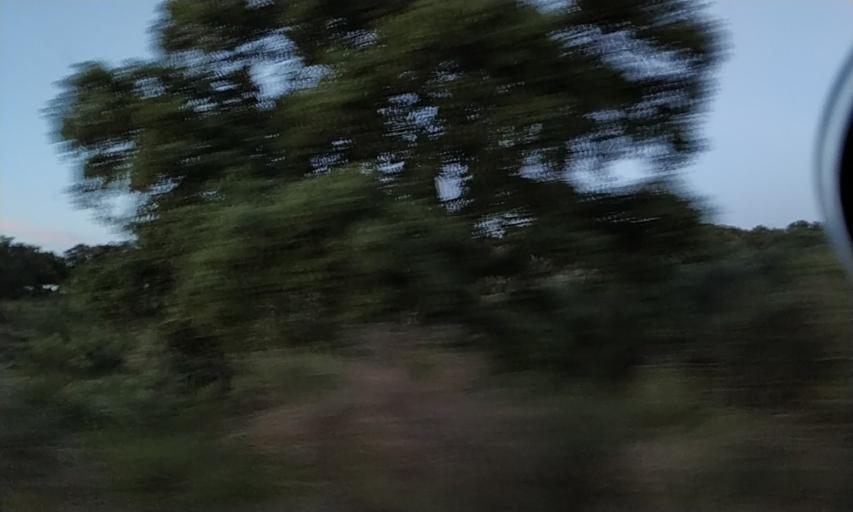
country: ES
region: Extremadura
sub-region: Provincia de Caceres
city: Piedras Albas
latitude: 39.7603
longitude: -6.9059
